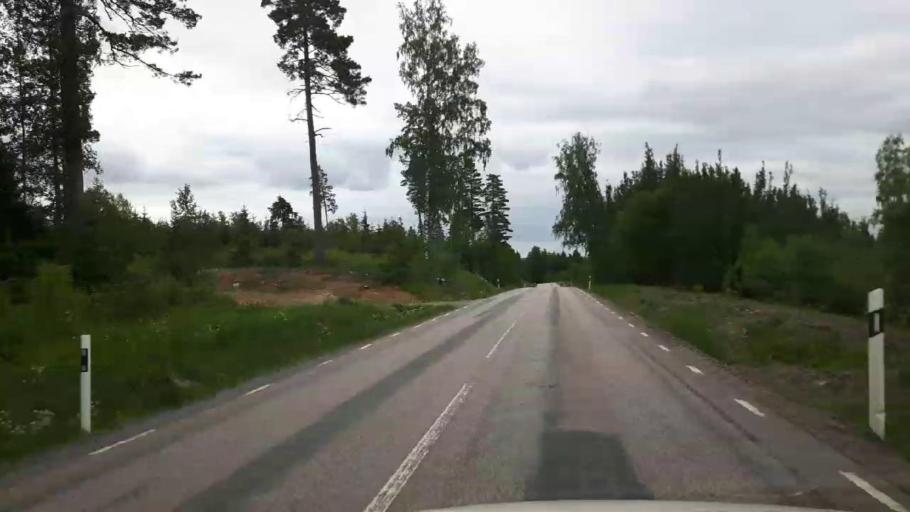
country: SE
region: Vaestmanland
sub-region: Kopings Kommun
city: Kolsva
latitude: 59.6394
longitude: 15.7958
